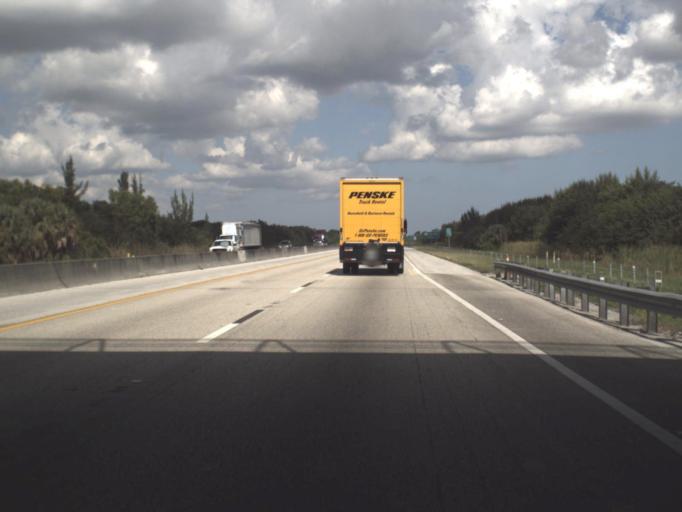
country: US
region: Florida
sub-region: Palm Beach County
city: Palm Beach Gardens
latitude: 26.8097
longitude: -80.1311
